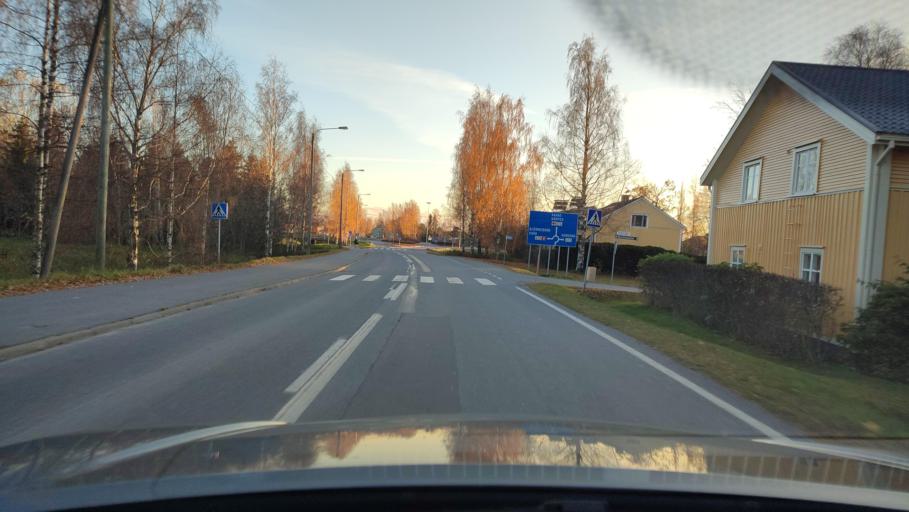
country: FI
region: Ostrobothnia
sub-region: Sydosterbotten
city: Naerpes
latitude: 62.4850
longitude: 21.3385
